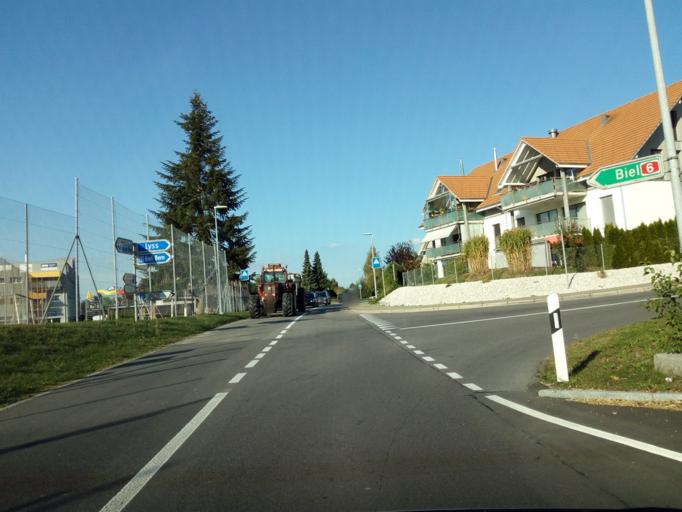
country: CH
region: Bern
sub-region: Seeland District
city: Schupfen
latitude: 47.0435
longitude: 7.3817
